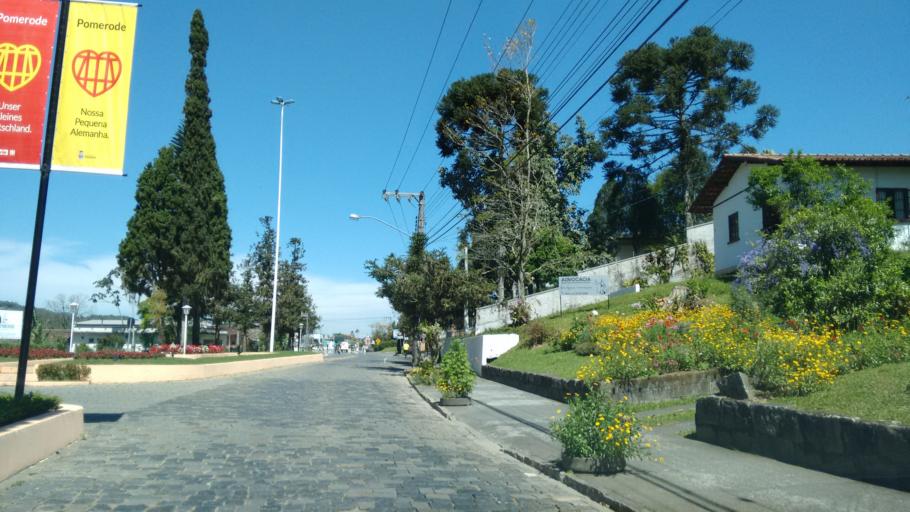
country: BR
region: Santa Catarina
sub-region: Pomerode
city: Pomerode
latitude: -26.7441
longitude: -49.1746
